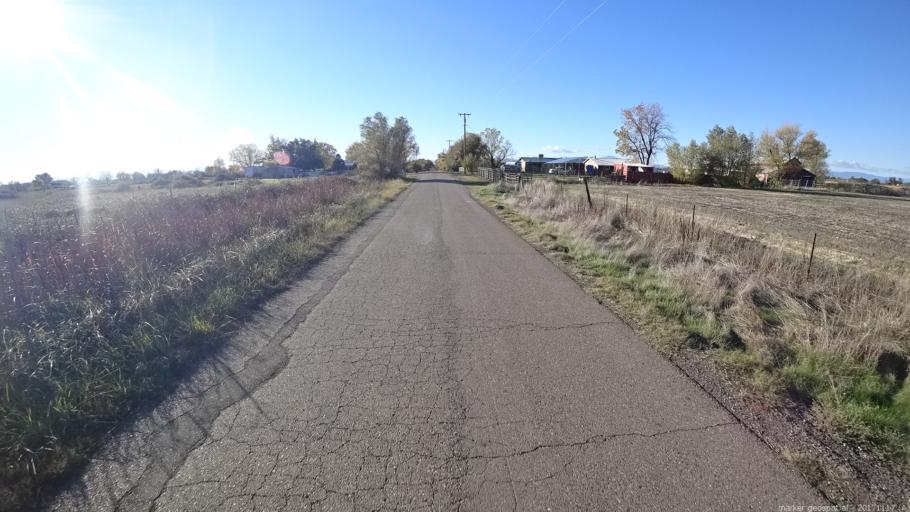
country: US
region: California
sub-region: Shasta County
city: Cottonwood
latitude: 40.3973
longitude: -122.2040
